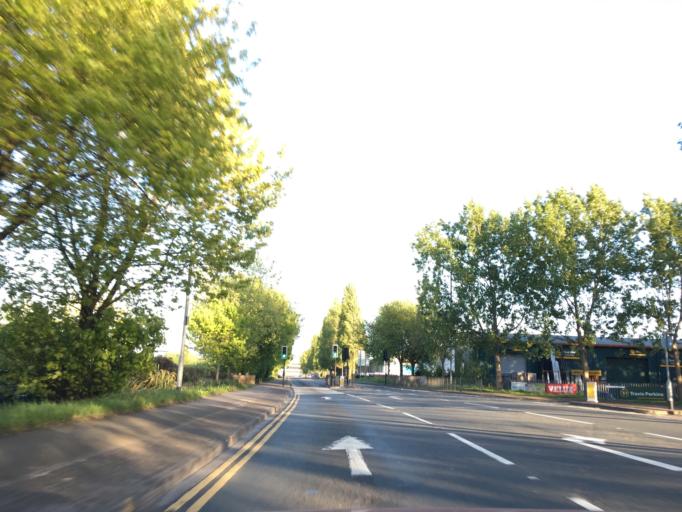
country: GB
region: Wales
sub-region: Newport
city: Newport
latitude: 51.5795
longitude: -2.9846
